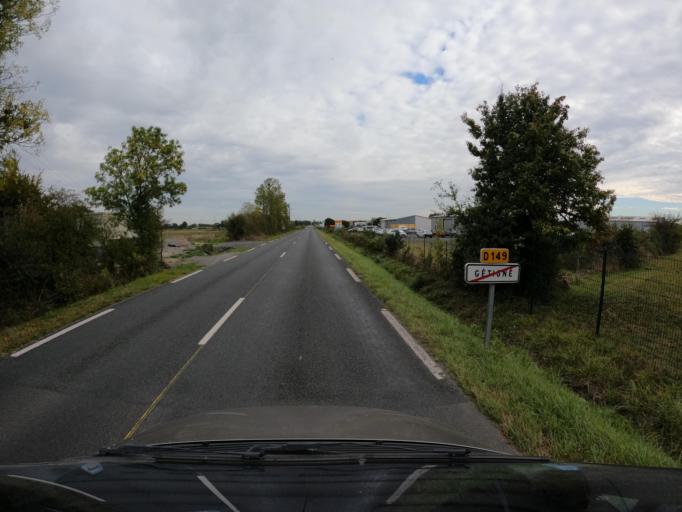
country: FR
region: Pays de la Loire
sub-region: Departement de la Loire-Atlantique
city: Getigne
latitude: 47.0762
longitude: -1.2347
